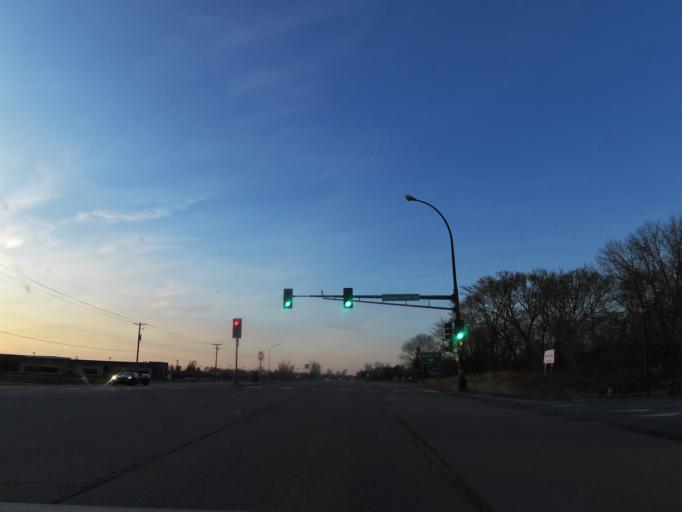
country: US
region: Minnesota
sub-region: Hennepin County
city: Eden Prairie
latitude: 44.8382
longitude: -93.4394
